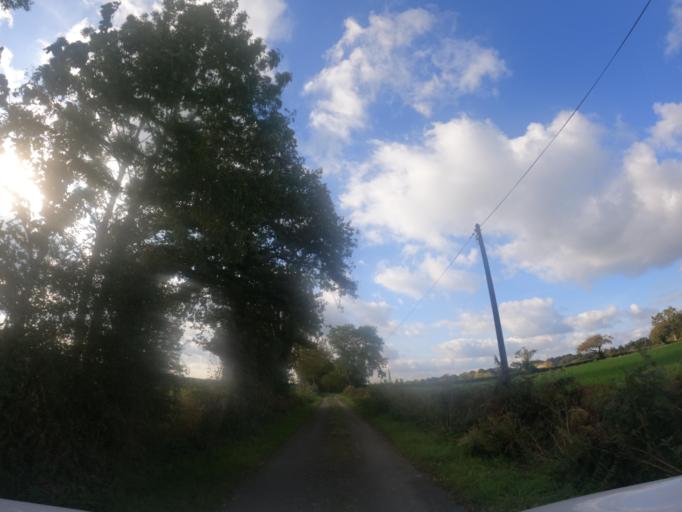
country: FR
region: Poitou-Charentes
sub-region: Departement des Deux-Sevres
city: Courlay
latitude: 46.7954
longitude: -0.6087
